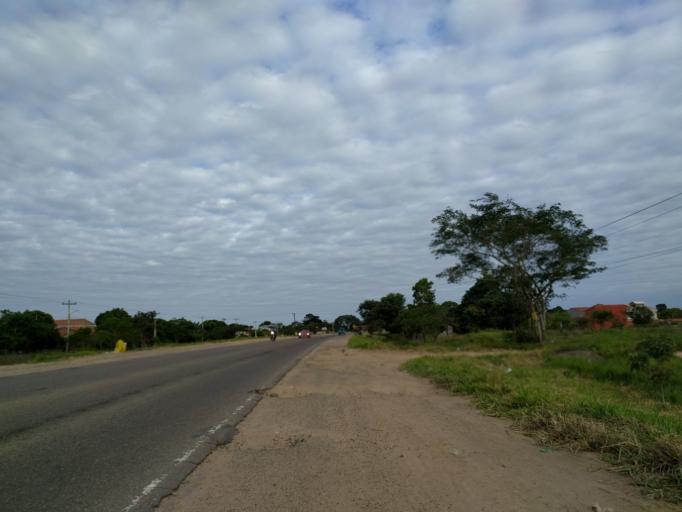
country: BO
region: Santa Cruz
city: Santa Rita
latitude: -17.8760
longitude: -63.2693
